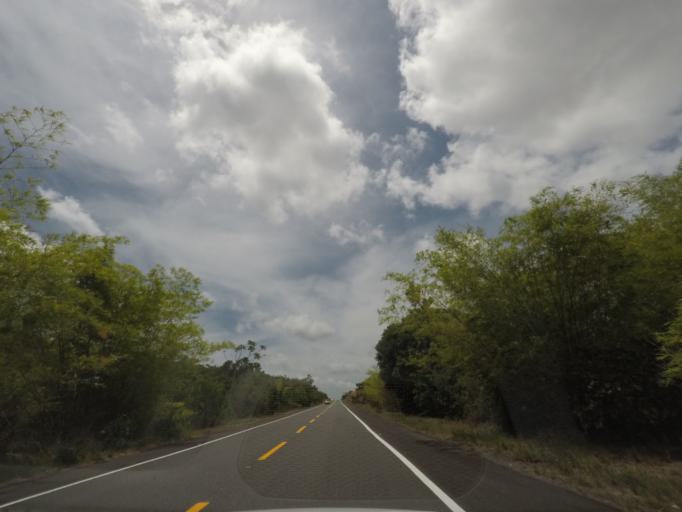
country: BR
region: Bahia
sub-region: Conde
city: Conde
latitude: -11.6804
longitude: -37.5649
